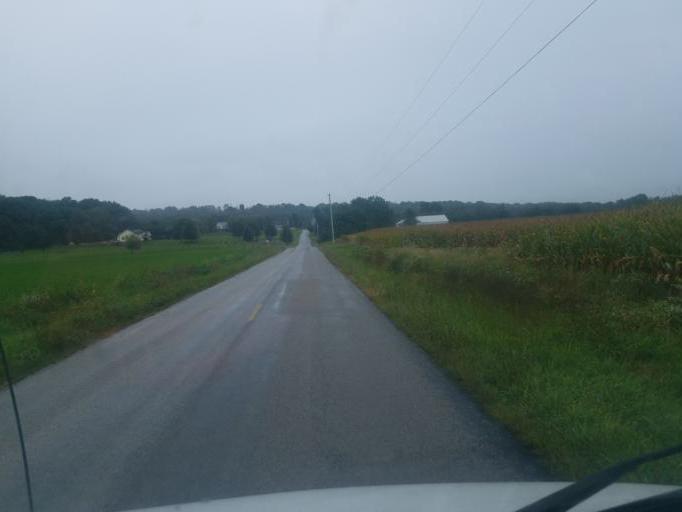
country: US
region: Ohio
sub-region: Medina County
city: Seville
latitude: 40.9824
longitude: -81.8473
